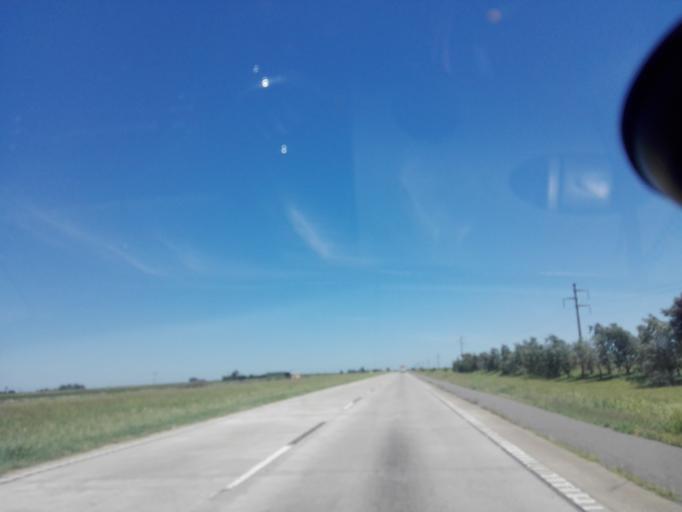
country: AR
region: Santa Fe
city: Canada de Gomez
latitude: -32.8613
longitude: -61.3039
